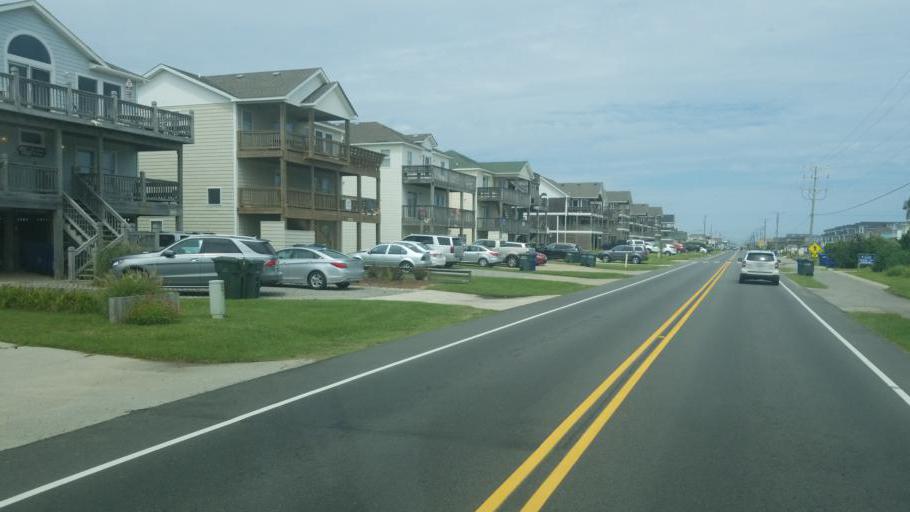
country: US
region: North Carolina
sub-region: Dare County
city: Nags Head
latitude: 35.9827
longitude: -75.6386
